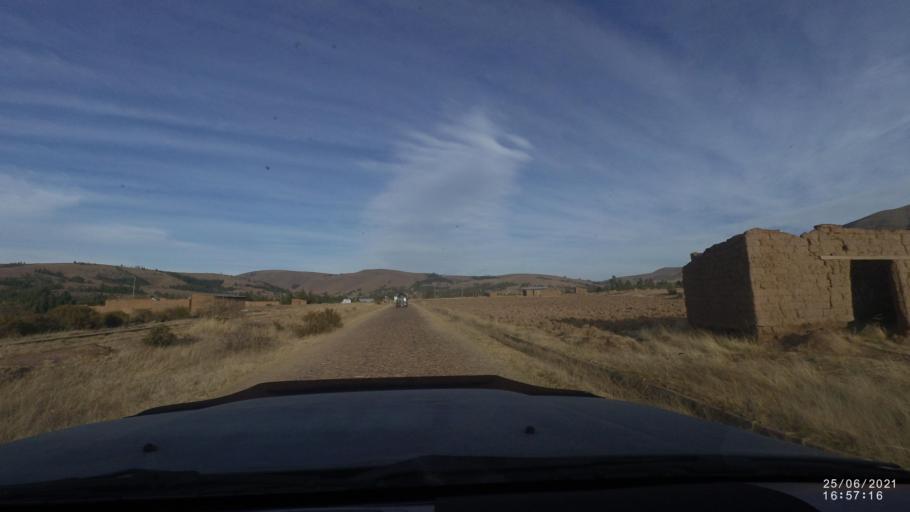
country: BO
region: Cochabamba
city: Arani
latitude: -17.8284
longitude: -65.7626
